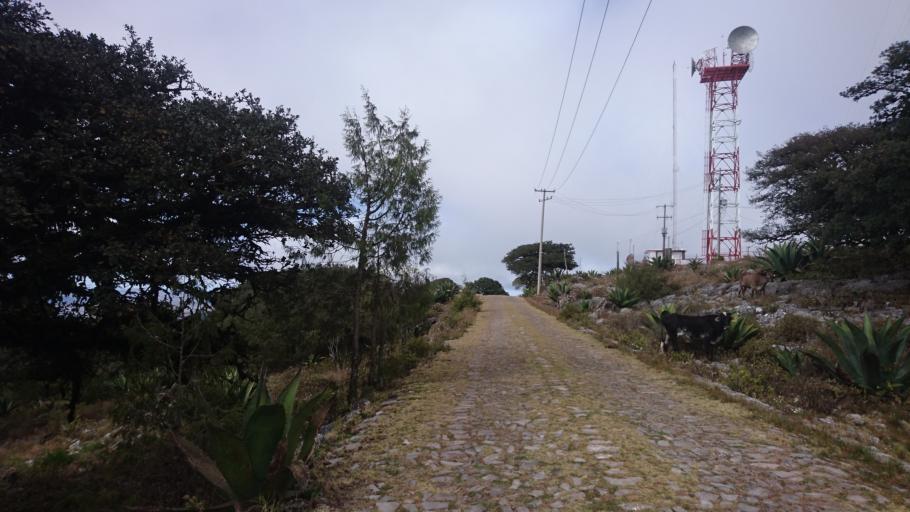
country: MX
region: San Luis Potosi
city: Zaragoza
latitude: 22.0670
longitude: -100.6473
